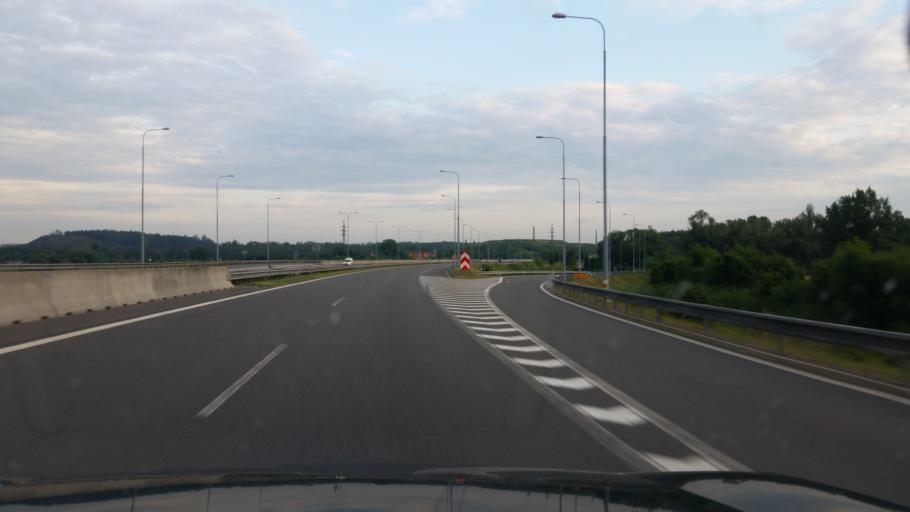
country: PL
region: Silesian Voivodeship
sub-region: Powiat raciborski
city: Chalupki
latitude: 49.8843
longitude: 18.3059
